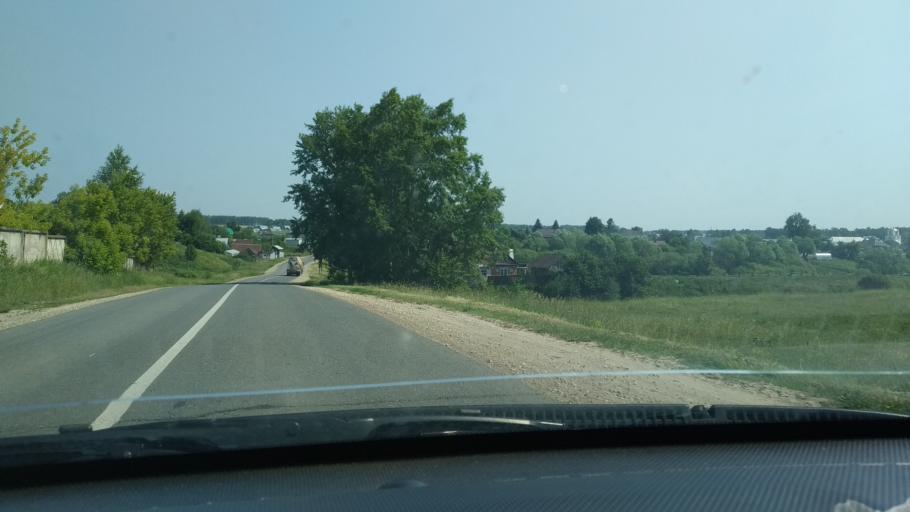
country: RU
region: Tatarstan
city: Osinovo
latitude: 55.9793
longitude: 48.7890
